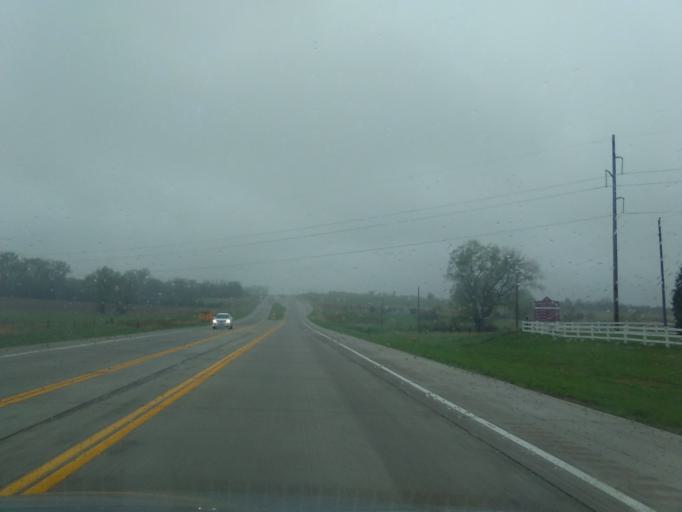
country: US
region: Nebraska
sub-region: Madison County
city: Norfolk
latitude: 42.0701
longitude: -97.3387
